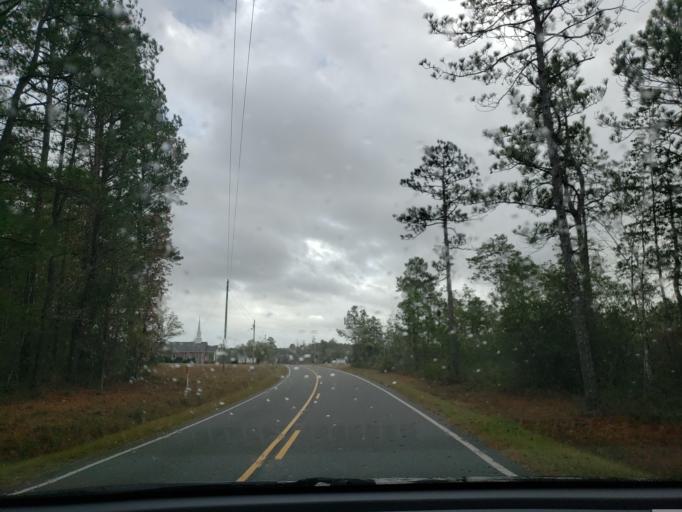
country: US
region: North Carolina
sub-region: Onslow County
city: Richlands
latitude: 34.7261
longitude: -77.6262
